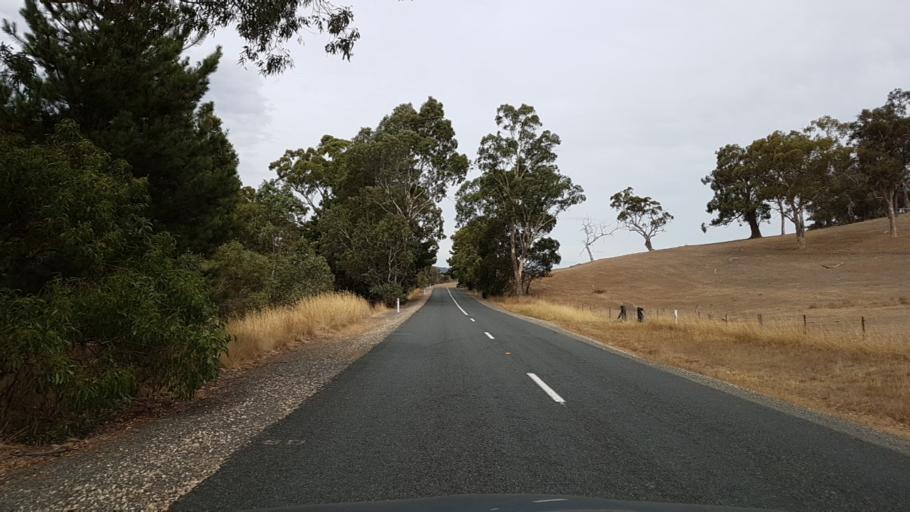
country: AU
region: South Australia
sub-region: Adelaide Hills
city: Birdwood
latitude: -34.7846
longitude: 138.9369
